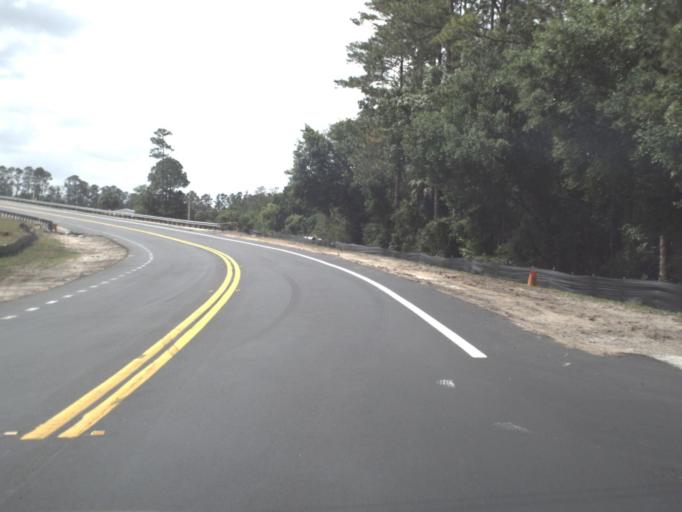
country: US
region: Florida
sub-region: Flagler County
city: Bunnell
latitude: 29.4716
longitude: -81.2636
